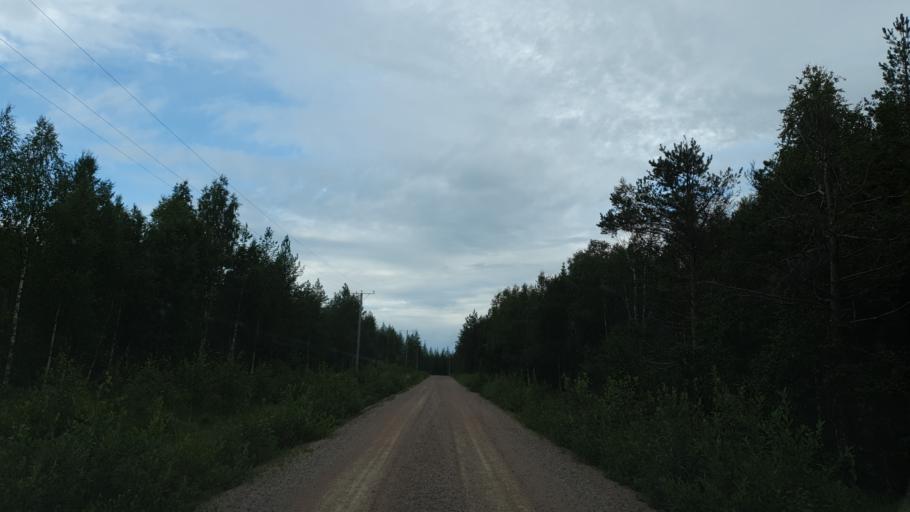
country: FI
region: Kainuu
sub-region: Kehys-Kainuu
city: Suomussalmi
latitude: 64.4478
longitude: 28.9685
